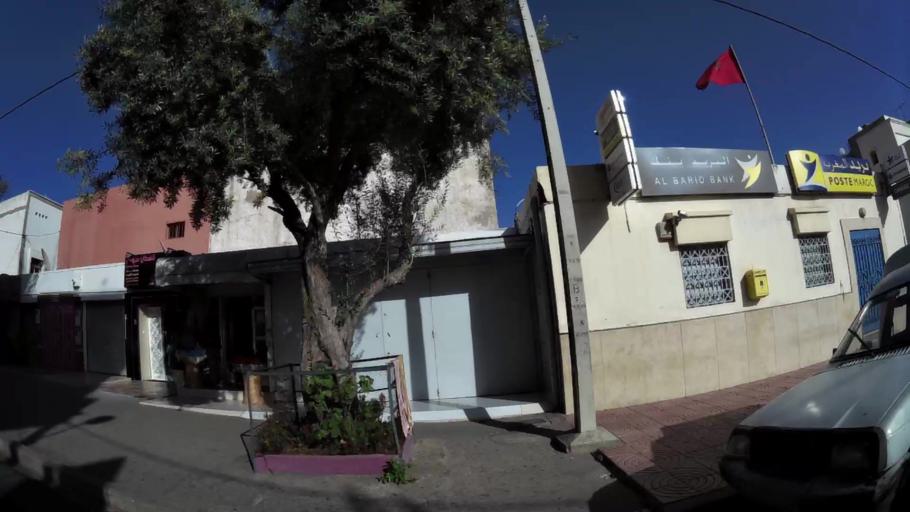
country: MA
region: Souss-Massa-Draa
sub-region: Agadir-Ida-ou-Tnan
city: Agadir
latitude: 30.4254
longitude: -9.5834
